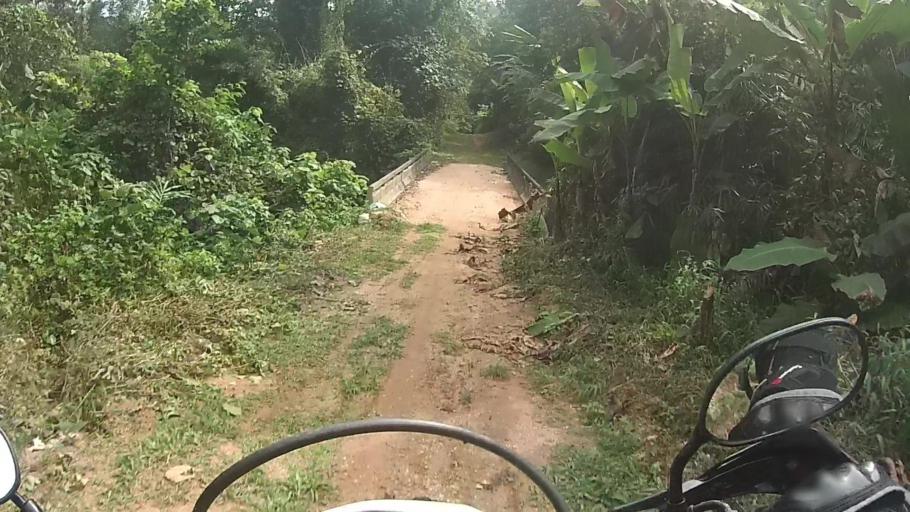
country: TH
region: Lampang
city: Mueang Pan
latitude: 18.8117
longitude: 99.3886
